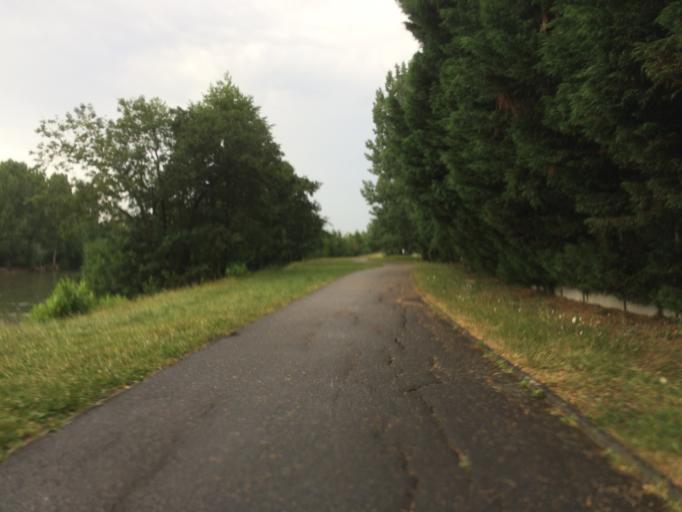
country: FR
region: Picardie
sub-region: Departement de l'Oise
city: Jaux
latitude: 49.3869
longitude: 2.7803
